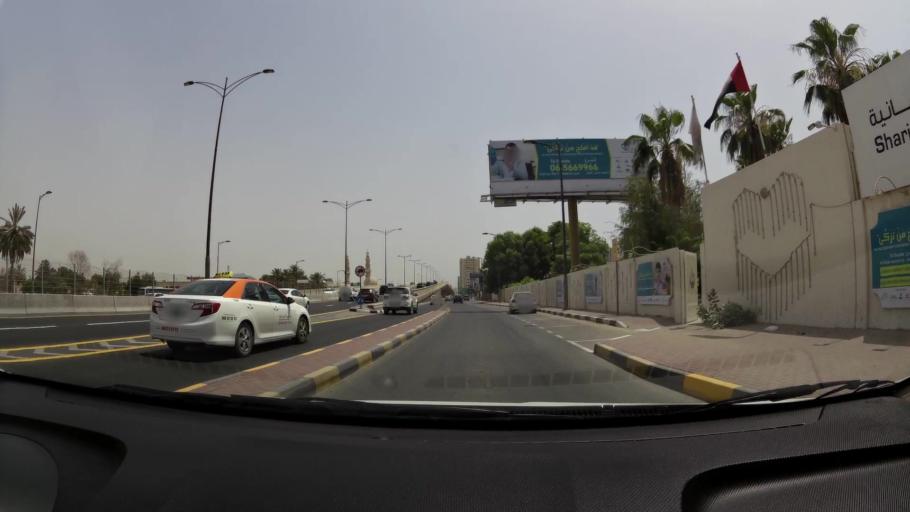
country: AE
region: Ash Shariqah
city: Sharjah
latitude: 25.3472
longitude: 55.4073
